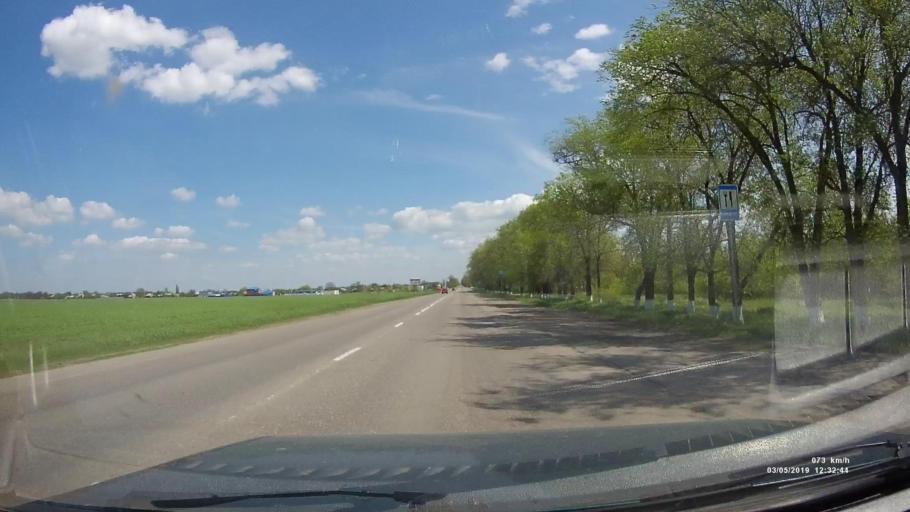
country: RU
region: Rostov
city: Semikarakorsk
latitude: 47.5124
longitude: 40.7643
